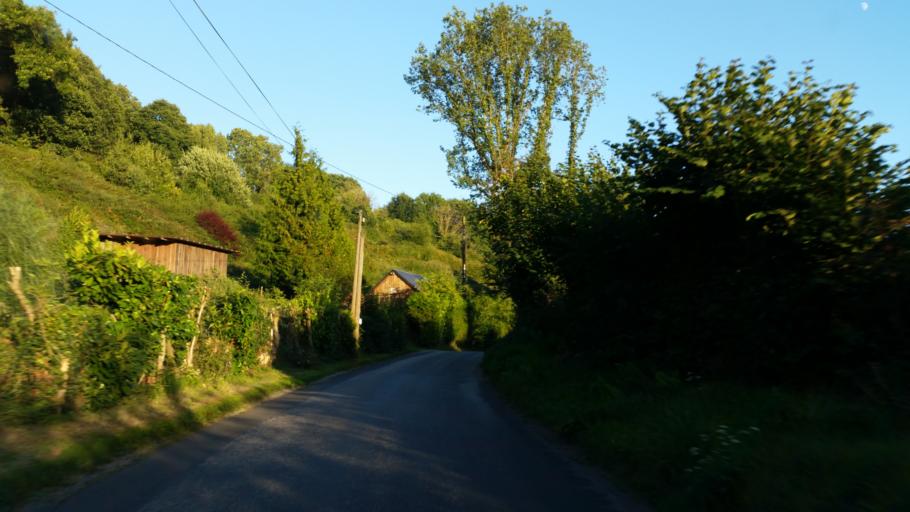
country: FR
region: Lower Normandy
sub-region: Departement du Calvados
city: Equemauville
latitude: 49.3953
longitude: 0.2248
